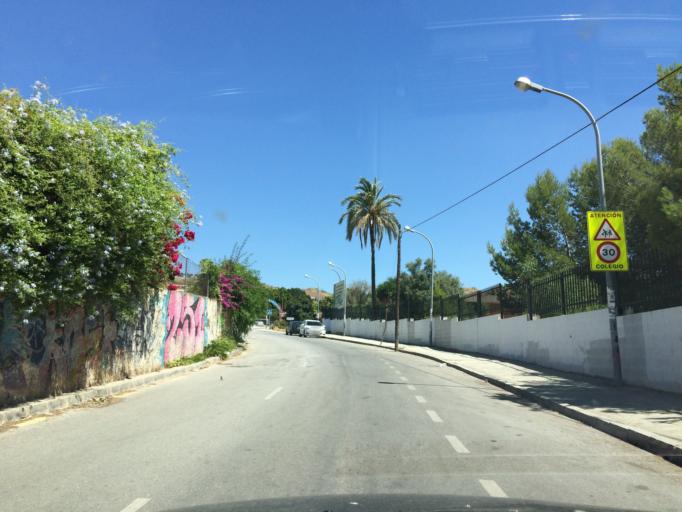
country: ES
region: Andalusia
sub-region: Provincia de Malaga
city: Malaga
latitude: 36.7335
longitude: -4.4666
